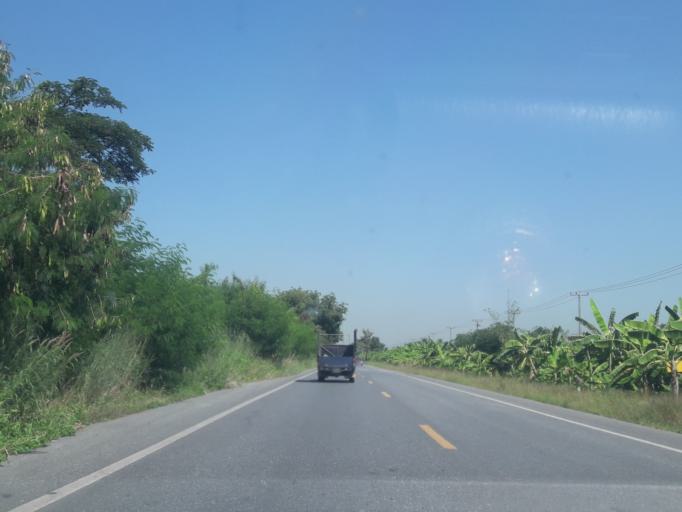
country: TH
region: Sara Buri
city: Nong Khae
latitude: 14.2560
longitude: 100.8234
